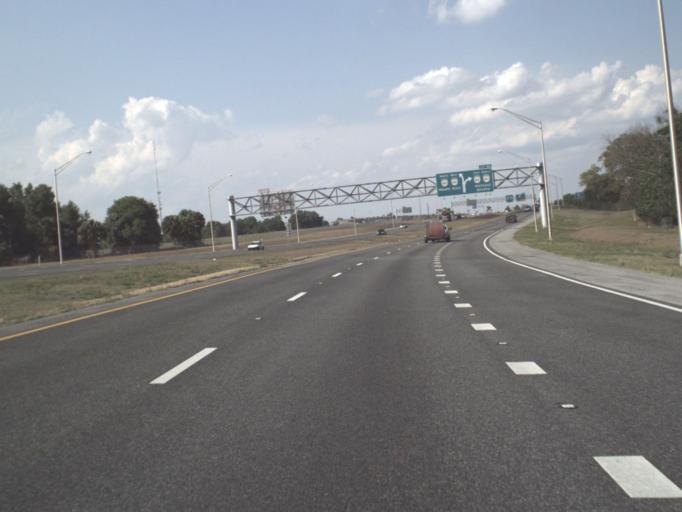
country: US
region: Florida
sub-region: Orange County
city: Paradise Heights
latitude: 28.6399
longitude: -81.5439
